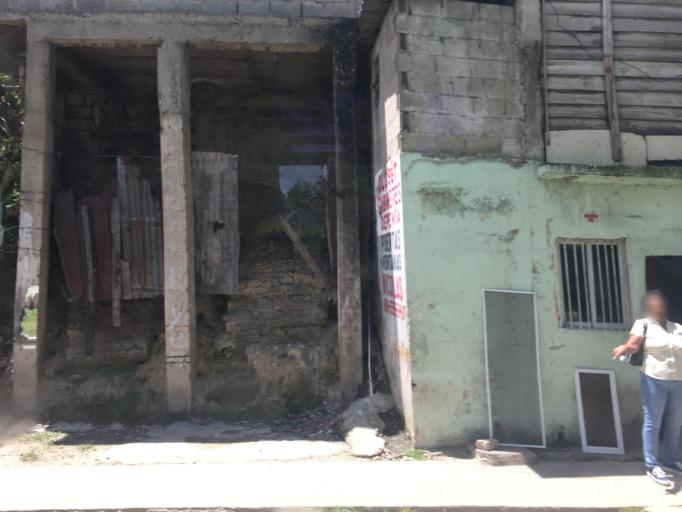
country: DO
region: Santiago
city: Santiago de los Caballeros
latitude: 19.4426
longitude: -70.7106
